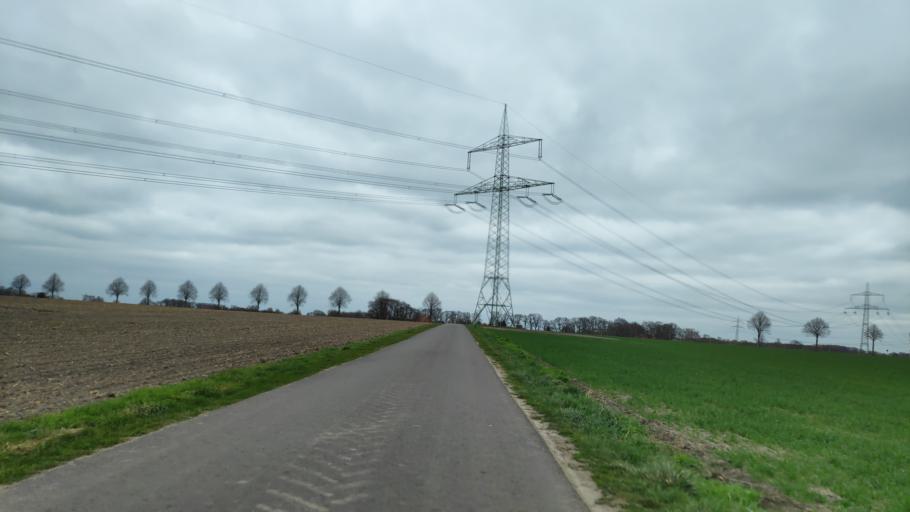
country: DE
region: North Rhine-Westphalia
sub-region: Regierungsbezirk Detmold
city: Minden
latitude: 52.3454
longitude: 8.8553
